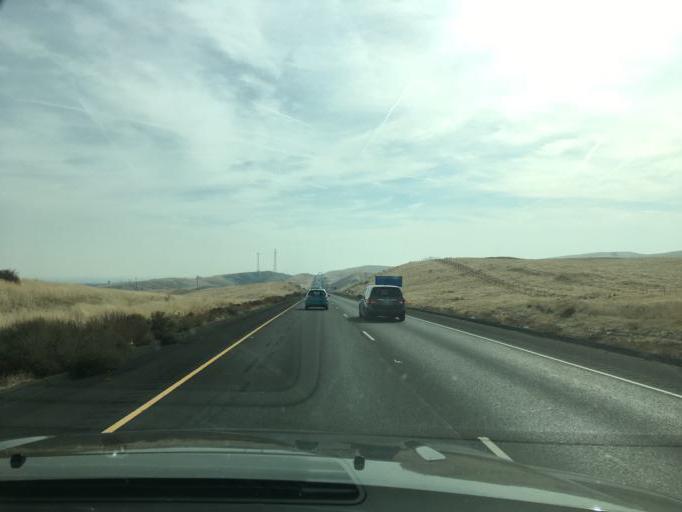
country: US
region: California
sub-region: Kings County
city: Kettleman City
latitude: 35.9964
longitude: -119.9756
